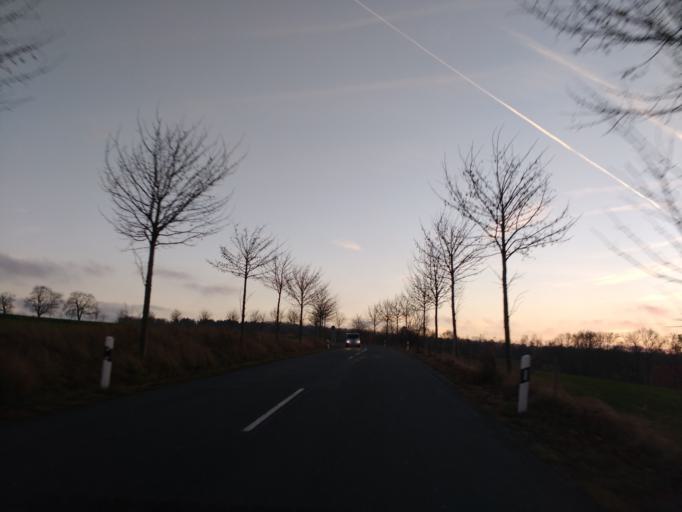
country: DE
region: North Rhine-Westphalia
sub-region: Regierungsbezirk Detmold
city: Paderborn
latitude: 51.6932
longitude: 8.7990
